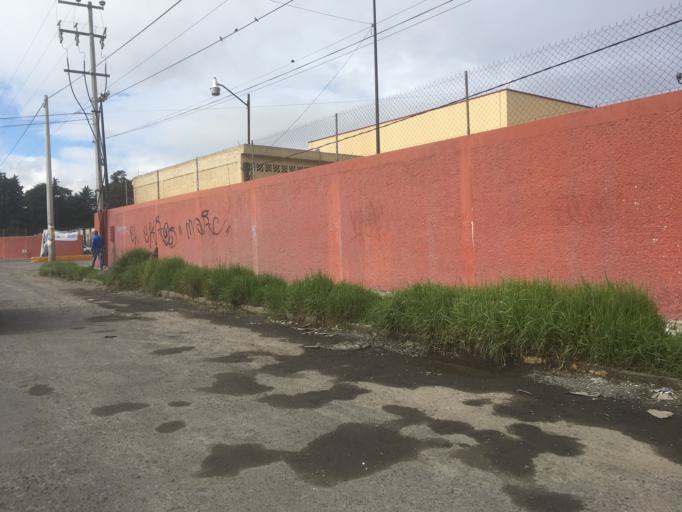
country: MX
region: Mexico
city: Santa Maria Totoltepec
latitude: 19.2952
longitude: -99.5942
